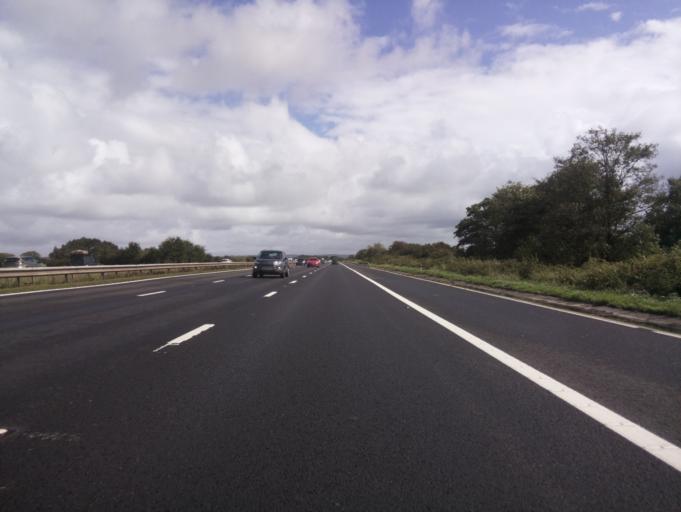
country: GB
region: England
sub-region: North Somerset
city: Kingston Seymour
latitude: 51.3829
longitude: -2.8733
